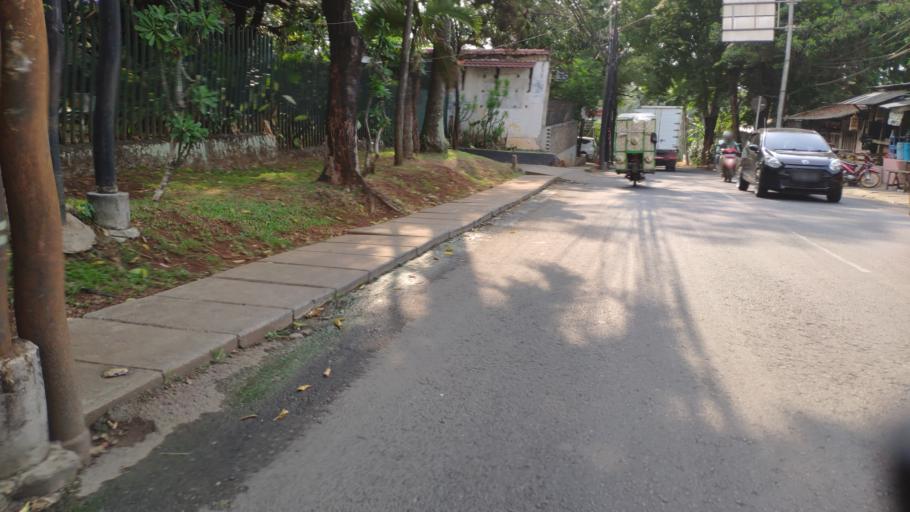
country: ID
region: West Java
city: Pamulang
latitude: -6.3108
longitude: 106.8129
